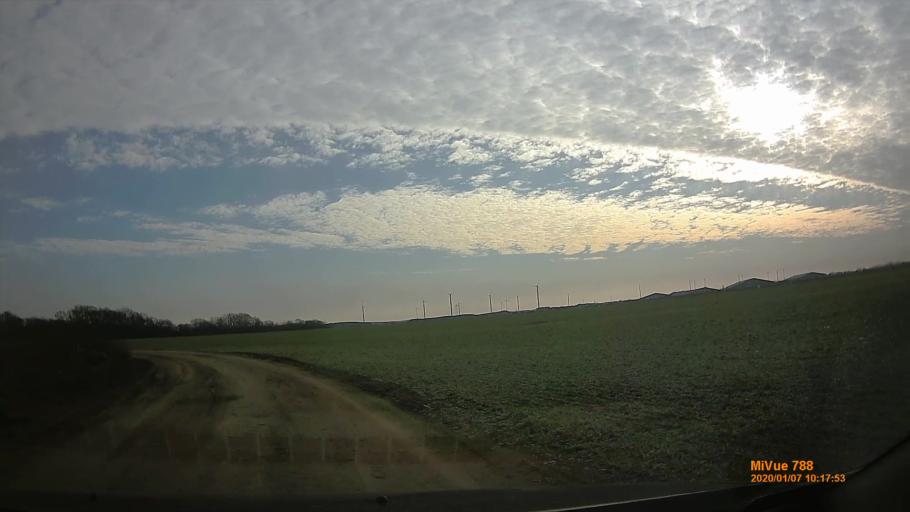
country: HU
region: Gyor-Moson-Sopron
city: Rajka
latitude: 47.9154
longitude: 17.1923
